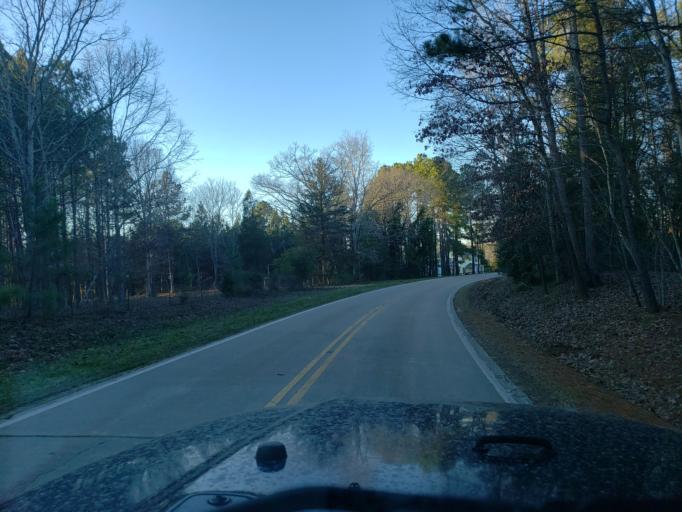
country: US
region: South Carolina
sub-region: Cherokee County
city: Blacksburg
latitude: 35.0427
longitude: -81.4130
